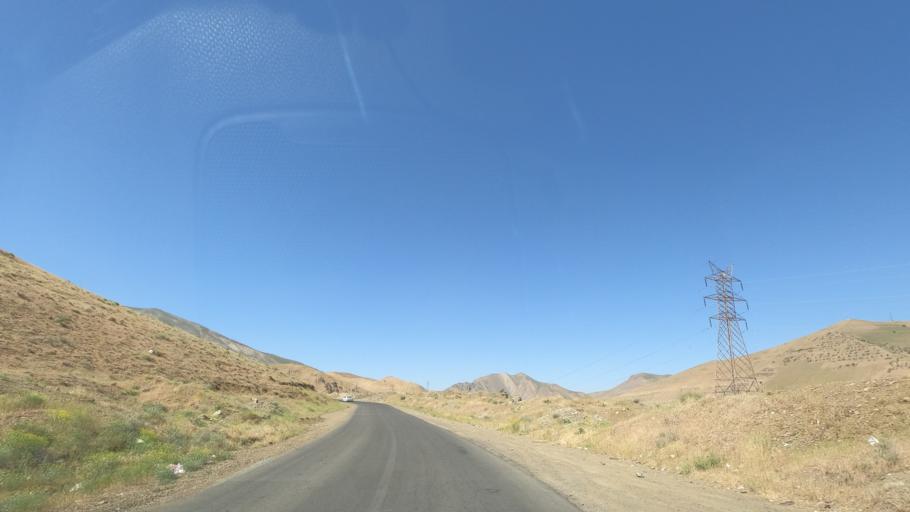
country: IR
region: Alborz
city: Karaj
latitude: 35.9403
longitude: 51.0798
